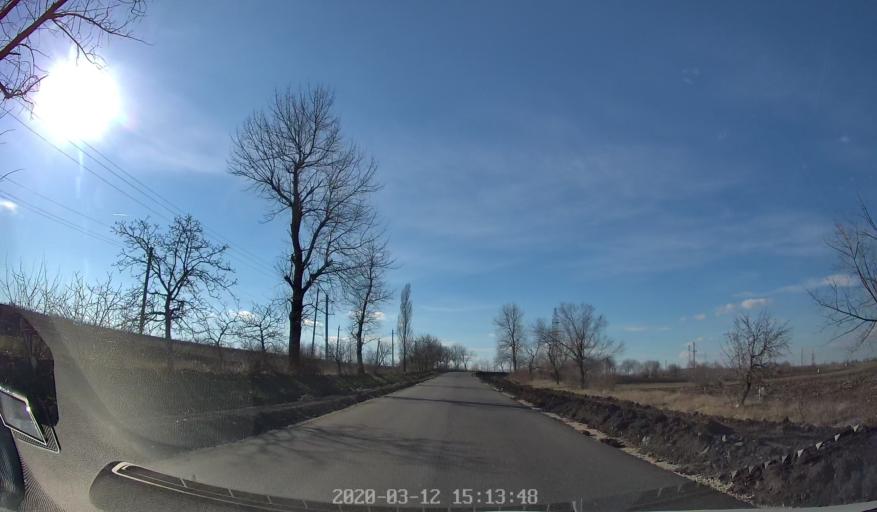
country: MD
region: Chisinau
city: Ciorescu
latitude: 47.2311
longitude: 28.9582
